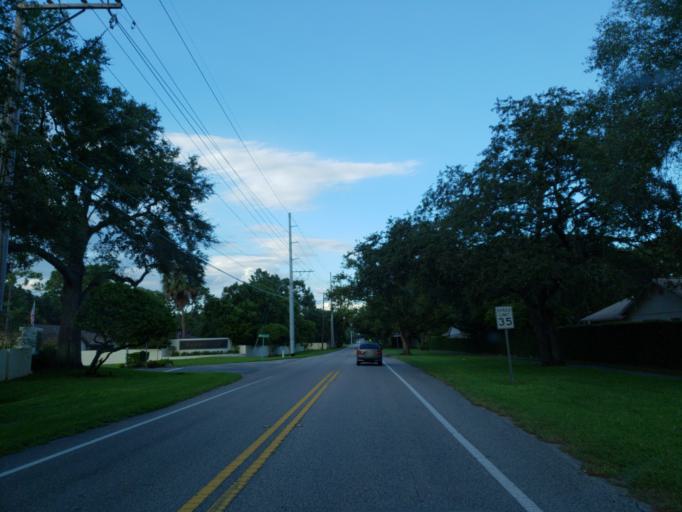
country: US
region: Florida
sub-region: Hillsborough County
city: Carrollwood Village
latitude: 28.0566
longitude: -82.5171
